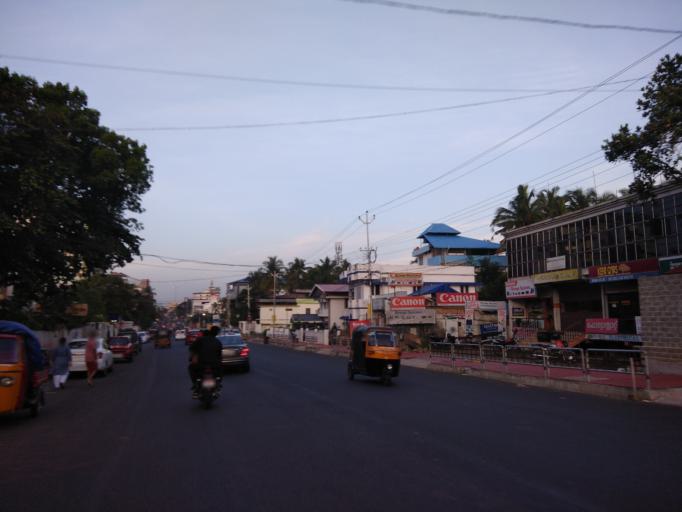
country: IN
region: Kerala
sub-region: Thrissur District
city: Trichur
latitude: 10.5218
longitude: 76.1976
